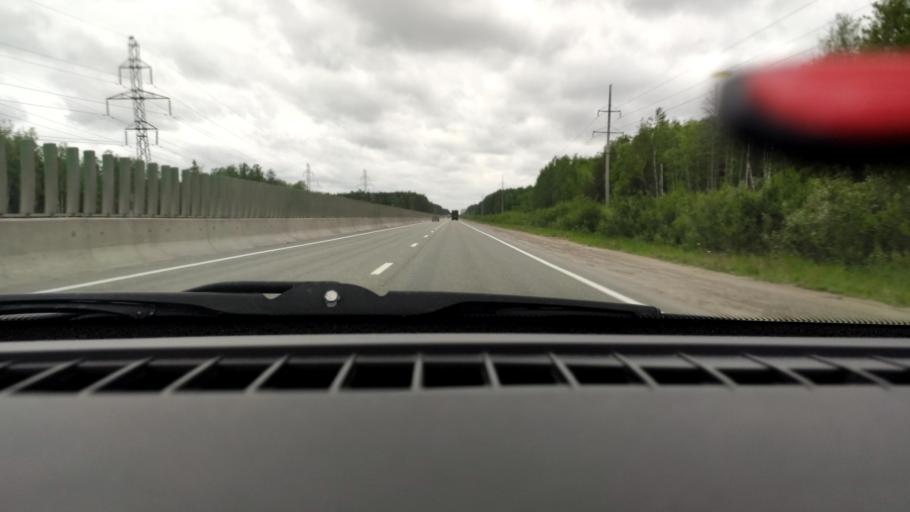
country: RU
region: Perm
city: Overyata
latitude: 58.0362
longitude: 55.9514
